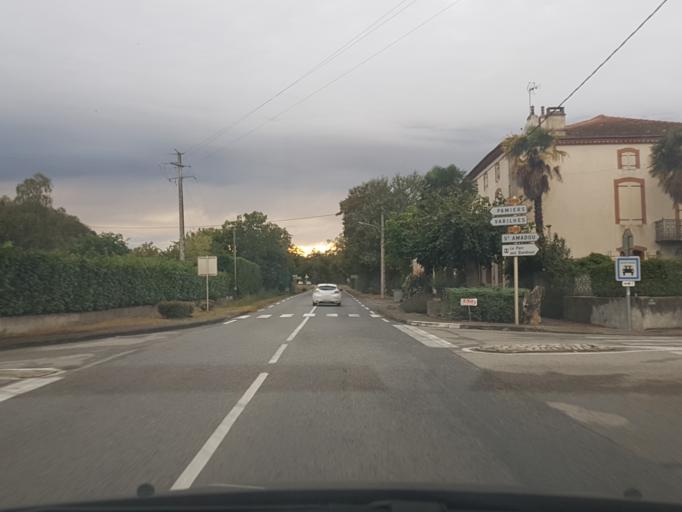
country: FR
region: Midi-Pyrenees
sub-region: Departement de l'Ariege
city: La Tour-du-Crieu
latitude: 43.0934
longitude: 1.7205
